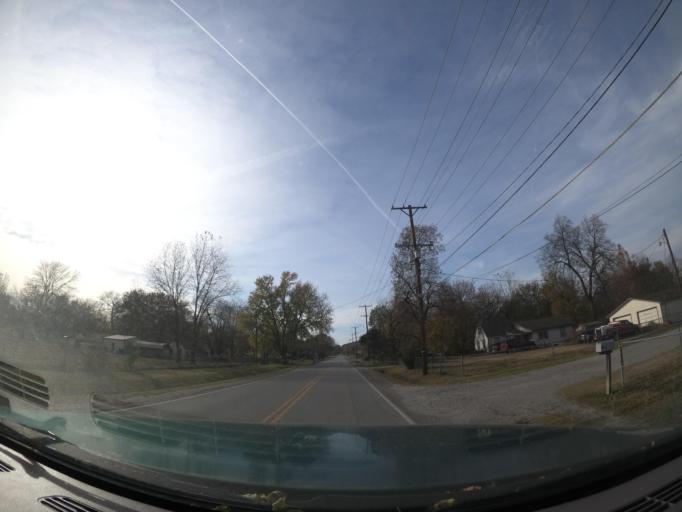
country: US
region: Oklahoma
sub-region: Tulsa County
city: Turley
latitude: 36.2496
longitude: -95.9706
